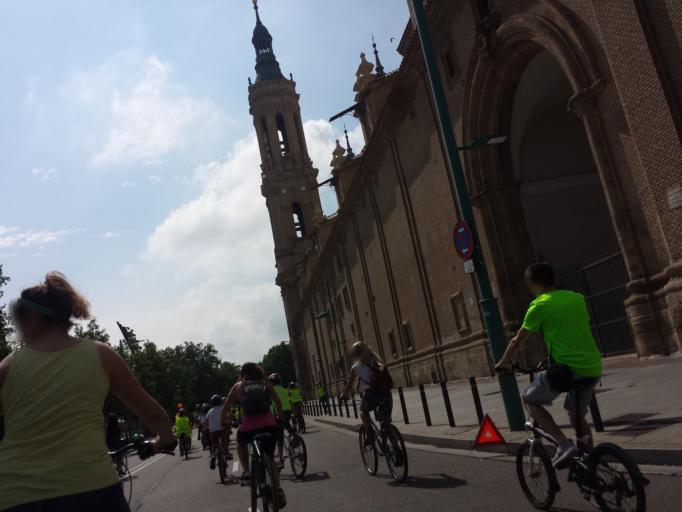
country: ES
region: Aragon
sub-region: Provincia de Zaragoza
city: Zaragoza
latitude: 41.6574
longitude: -0.8790
